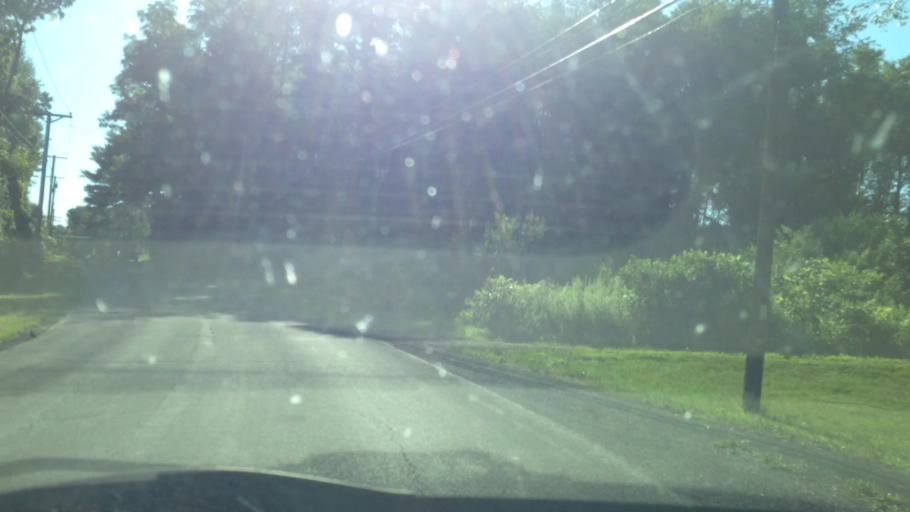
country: US
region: New York
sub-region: Ulster County
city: New Paltz
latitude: 41.7427
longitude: -74.0465
